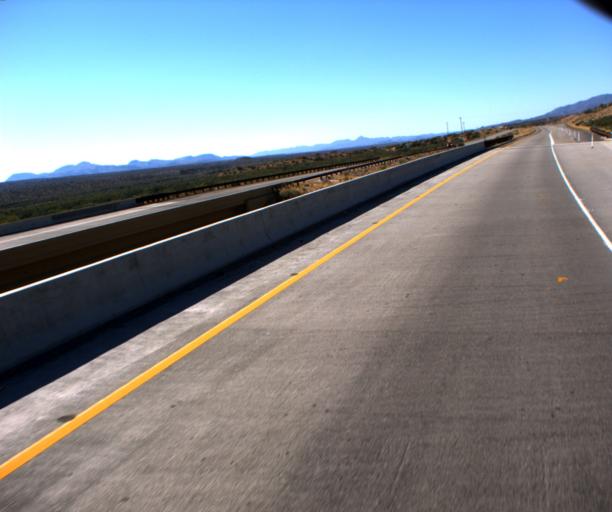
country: US
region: Arizona
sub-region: Yavapai County
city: Bagdad
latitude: 34.8196
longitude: -113.6265
